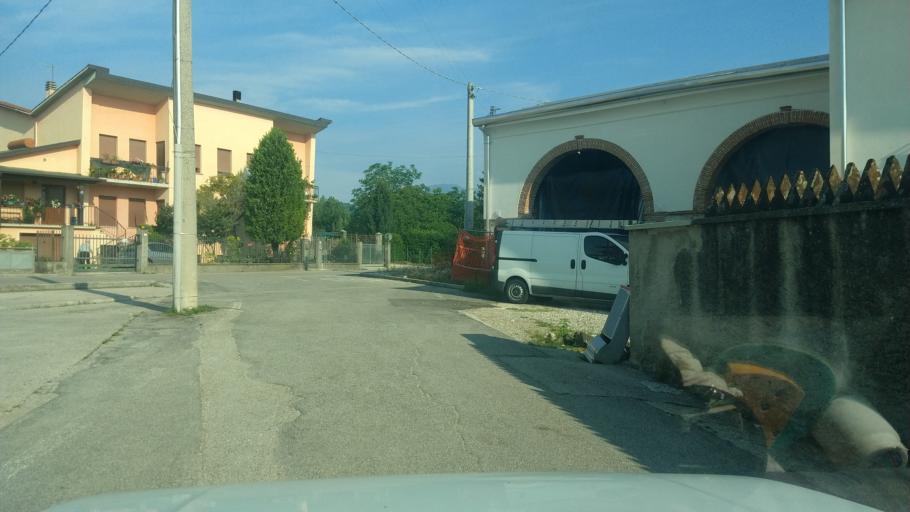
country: IT
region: Veneto
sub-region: Provincia di Vicenza
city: Mure
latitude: 45.7250
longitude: 11.6159
